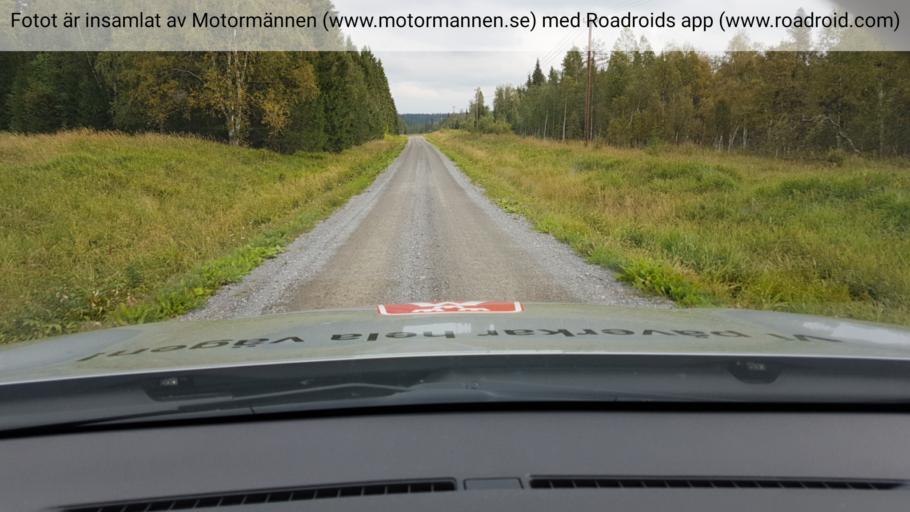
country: SE
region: Jaemtland
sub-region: Stroemsunds Kommun
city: Stroemsund
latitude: 63.7833
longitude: 15.2563
